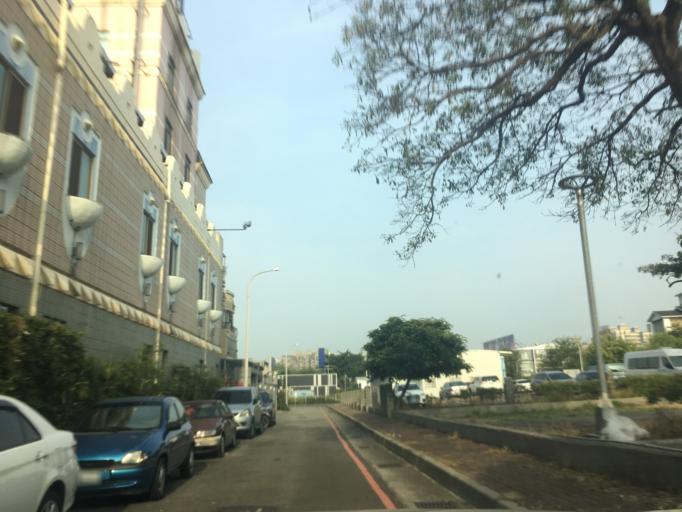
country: TW
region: Taiwan
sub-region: Taichung City
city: Taichung
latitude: 24.1899
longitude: 120.6888
